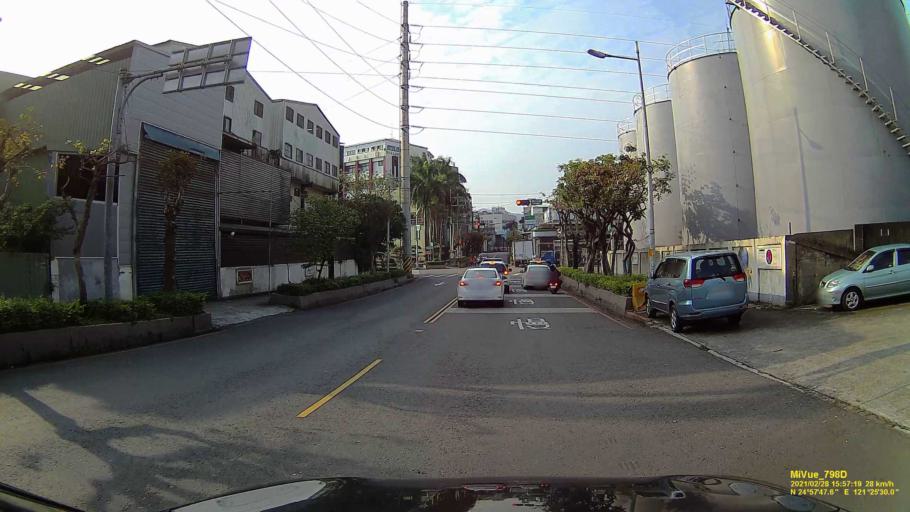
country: TW
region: Taipei
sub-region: Taipei
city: Banqiao
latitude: 24.9633
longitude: 121.4247
